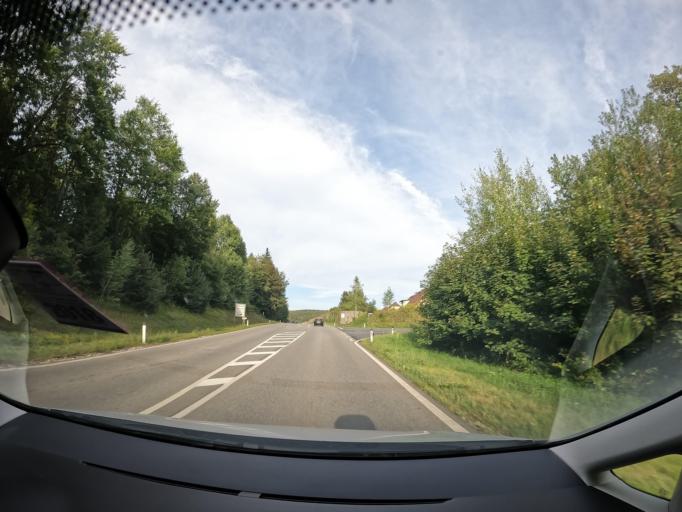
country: AT
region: Carinthia
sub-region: Politischer Bezirk Volkermarkt
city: Voelkermarkt
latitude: 46.6658
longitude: 14.6515
